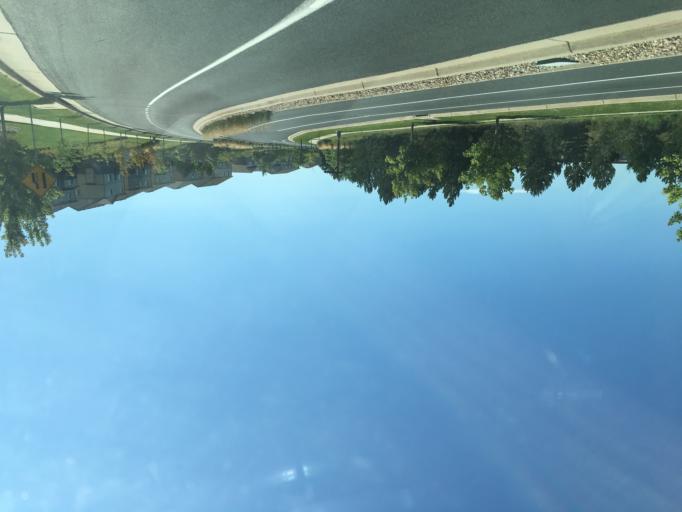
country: US
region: Colorado
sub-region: Douglas County
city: Parker
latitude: 39.5969
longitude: -104.6958
